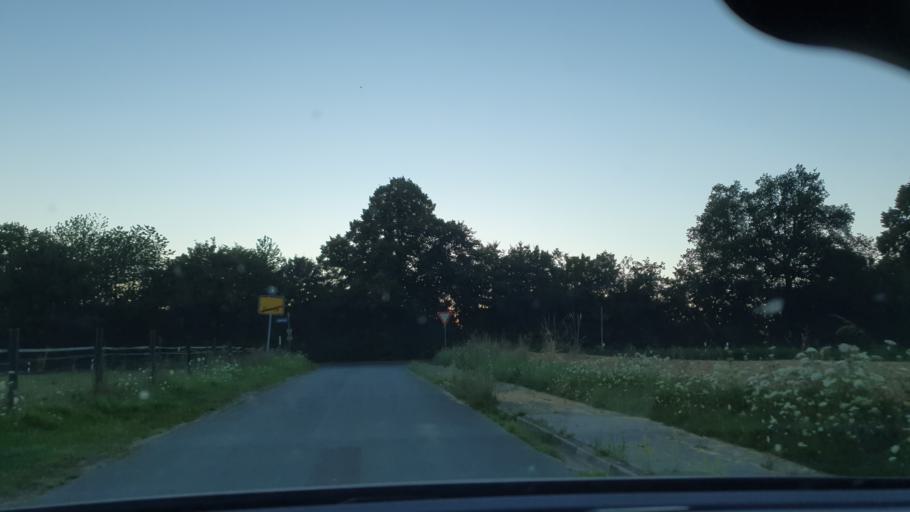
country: DE
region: North Rhine-Westphalia
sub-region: Regierungsbezirk Detmold
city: Rodinghausen
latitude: 52.2119
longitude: 8.5007
